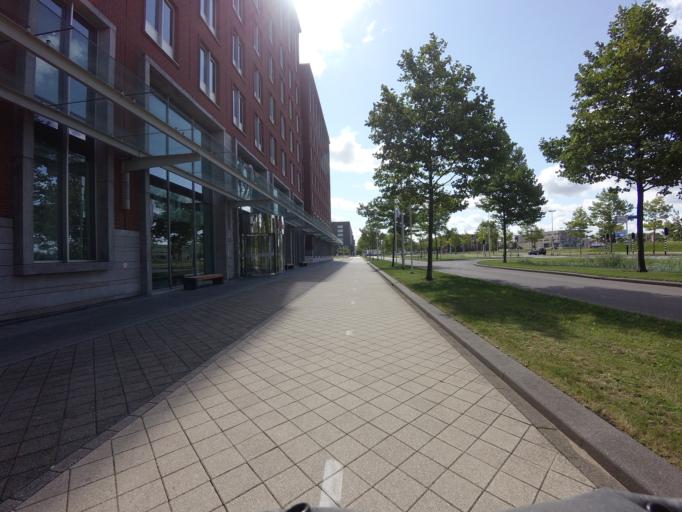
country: NL
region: Utrecht
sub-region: Gemeente Nieuwegein
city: Nieuwegein
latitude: 52.0701
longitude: 5.0802
